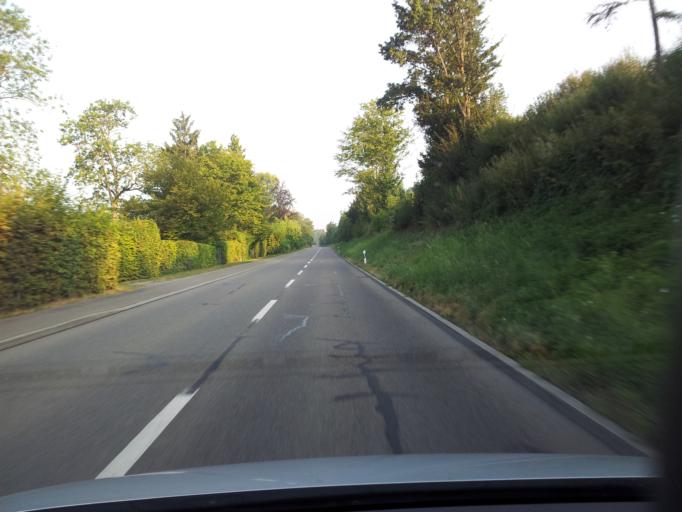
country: CH
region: Lucerne
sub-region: Sursee District
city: Eich
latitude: 47.1576
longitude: 8.1544
